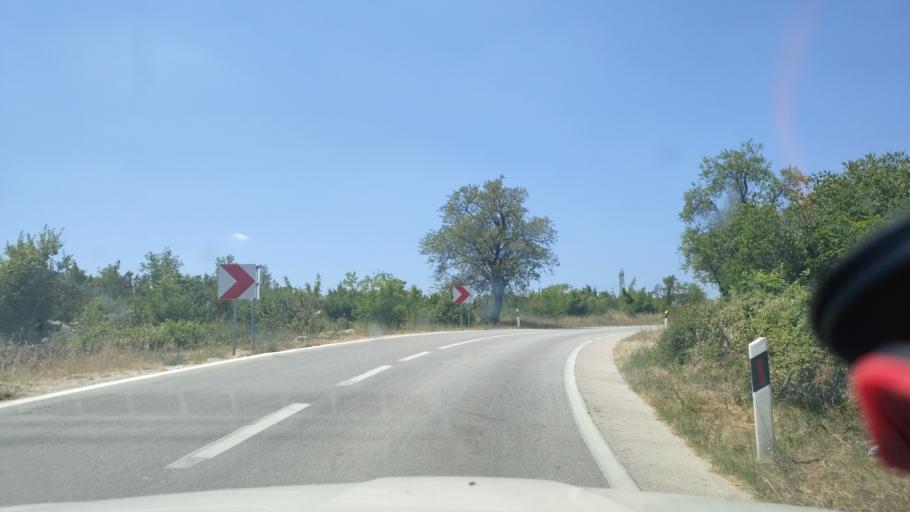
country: HR
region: Sibensko-Kniniska
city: Kistanje
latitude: 44.0002
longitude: 15.9927
